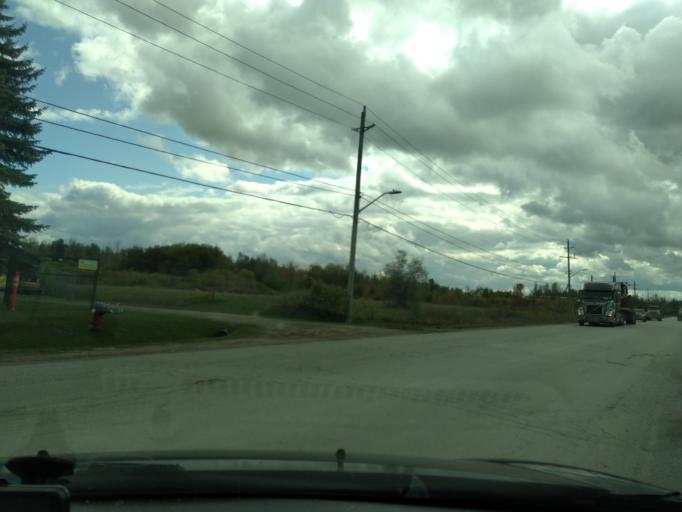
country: CA
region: Ontario
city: Bradford West Gwillimbury
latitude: 44.1363
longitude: -79.5557
